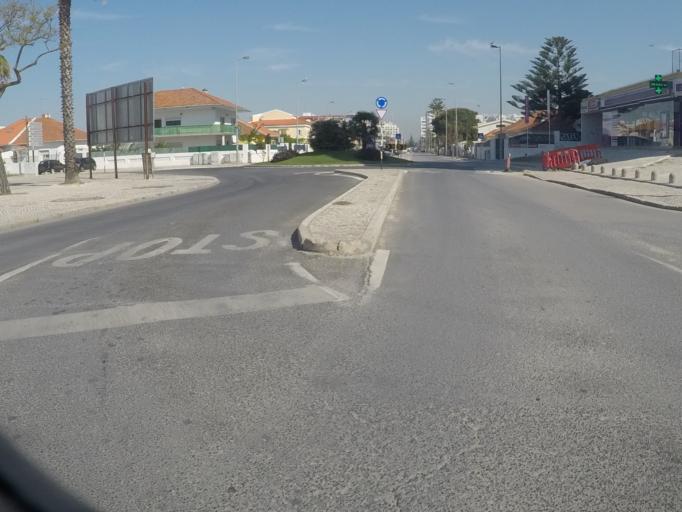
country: PT
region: Setubal
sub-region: Almada
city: Costa de Caparica
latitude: 38.6389
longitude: -9.2302
